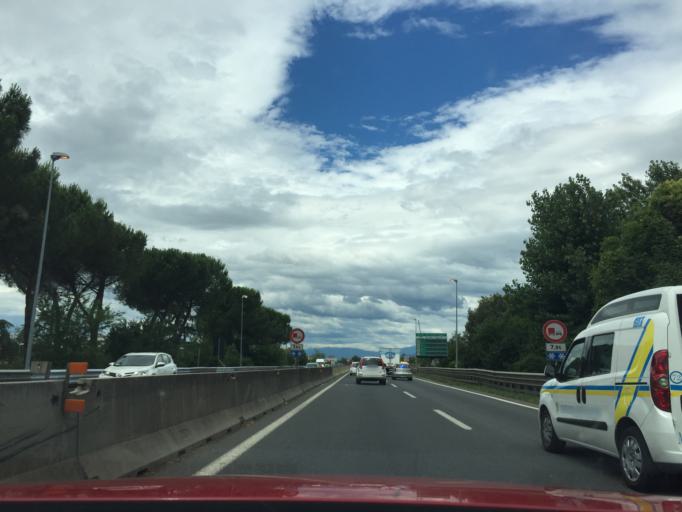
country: IT
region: Tuscany
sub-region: Province of Florence
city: Sesto Fiorentino
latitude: 43.8014
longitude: 11.2003
